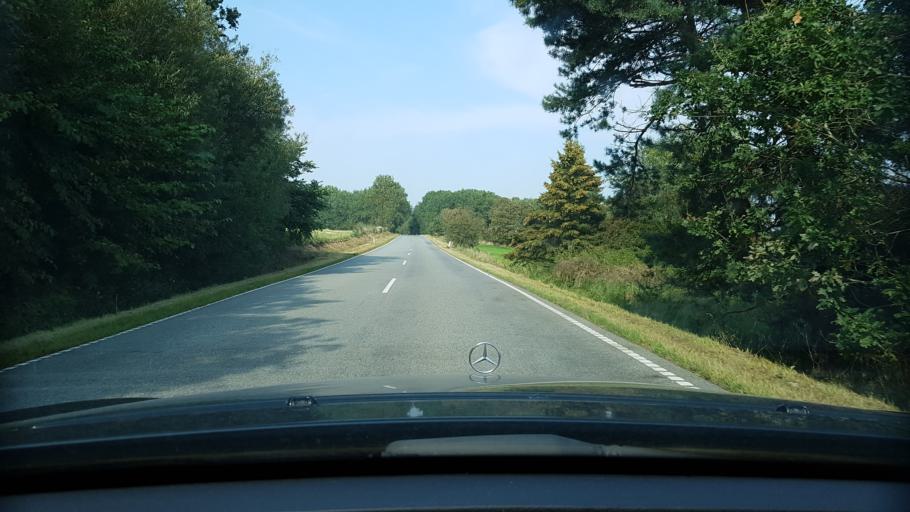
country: DK
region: North Denmark
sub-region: Alborg Kommune
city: Hals
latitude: 56.8930
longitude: 10.2611
